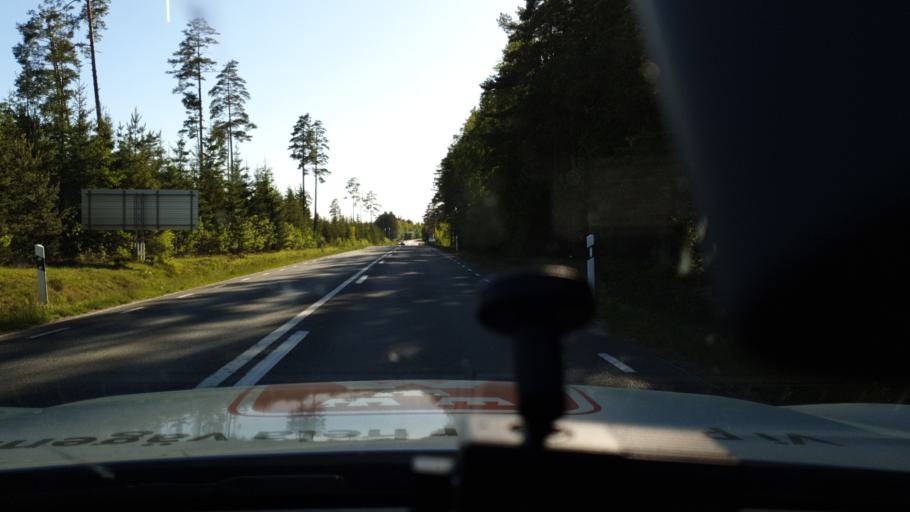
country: SE
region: Joenkoeping
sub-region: Vetlanda Kommun
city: Vetlanda
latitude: 57.4115
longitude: 14.9971
